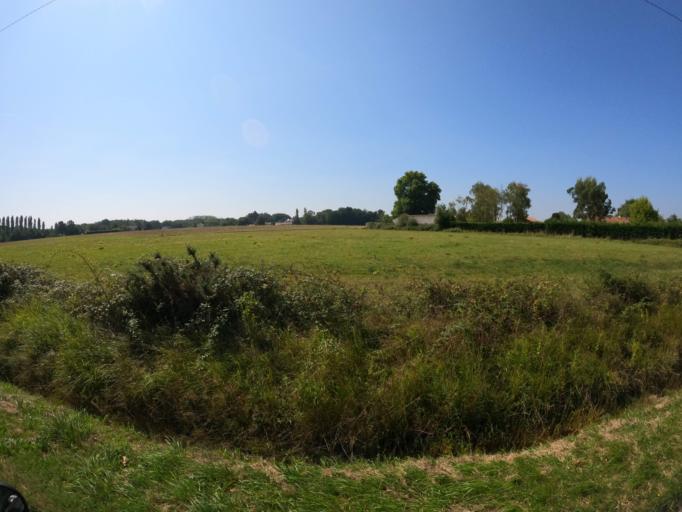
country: FR
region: Pays de la Loire
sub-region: Departement de la Loire-Atlantique
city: Pont-Saint-Martin
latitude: 47.1217
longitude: -1.5747
